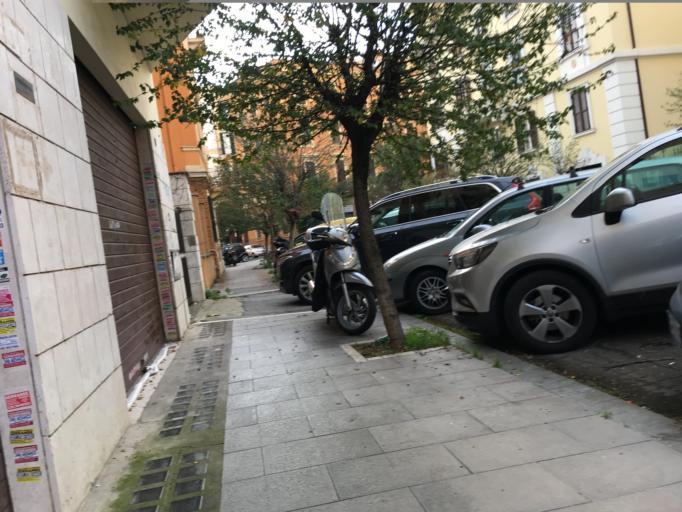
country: IT
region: Latium
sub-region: Citta metropolitana di Roma Capitale
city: Rome
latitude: 41.9099
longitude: 12.5172
